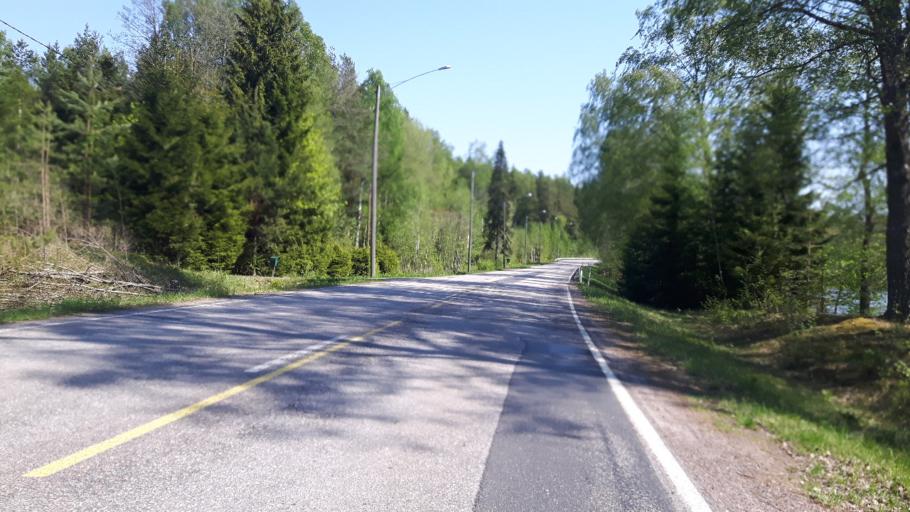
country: FI
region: Uusimaa
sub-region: Loviisa
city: Ruotsinpyhtaeae
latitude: 60.5001
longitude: 26.4495
